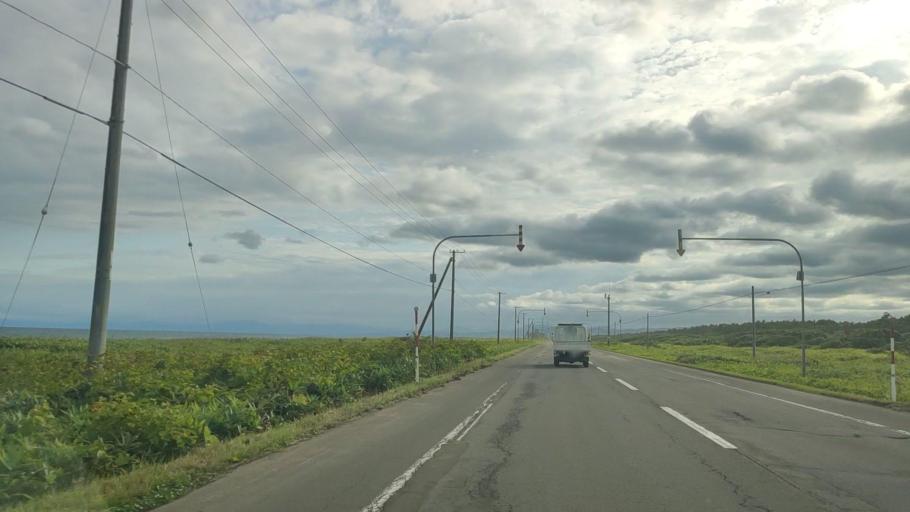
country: JP
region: Hokkaido
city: Niseko Town
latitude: 42.5666
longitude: 140.4386
